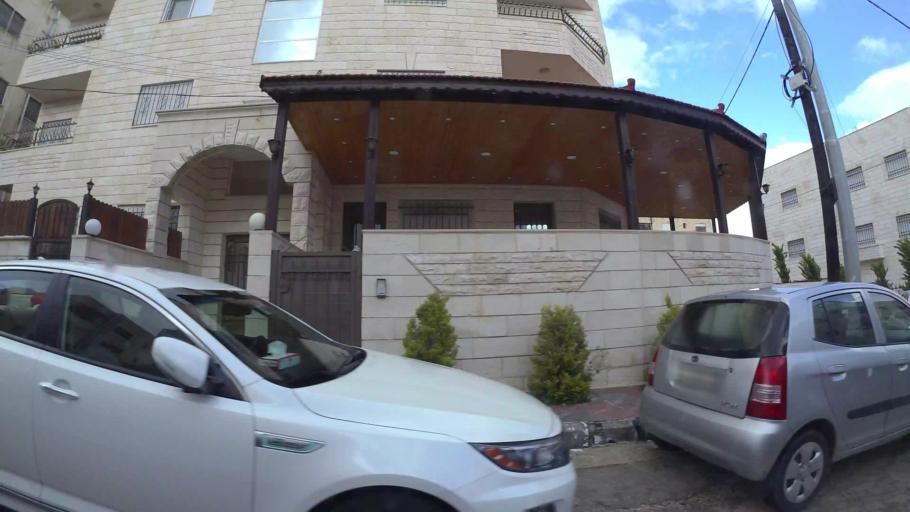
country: JO
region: Amman
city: Amman
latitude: 31.9991
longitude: 35.9228
